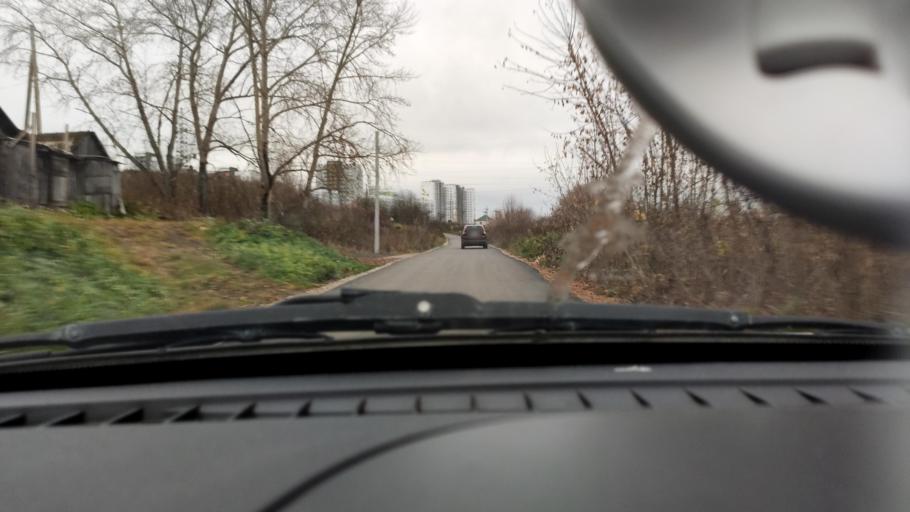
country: RU
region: Perm
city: Kondratovo
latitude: 57.9938
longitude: 56.1224
